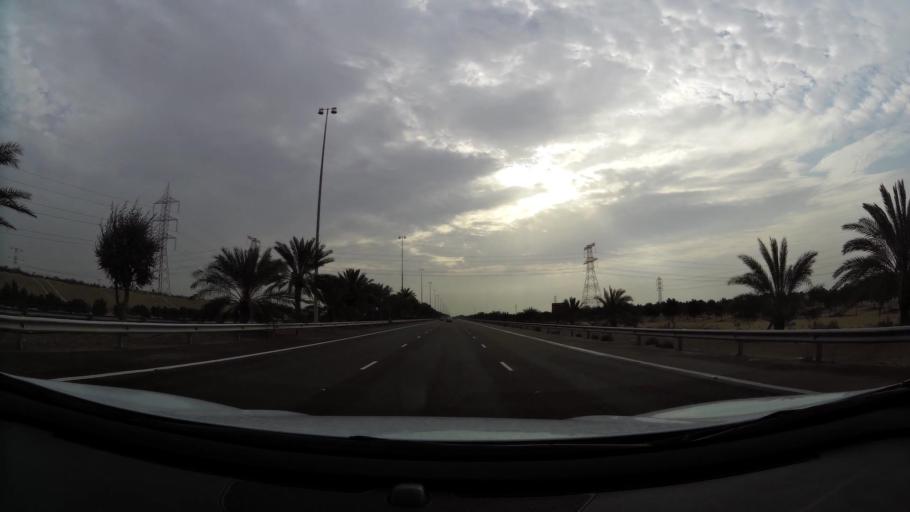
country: AE
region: Abu Dhabi
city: Abu Dhabi
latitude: 24.2275
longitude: 54.7903
